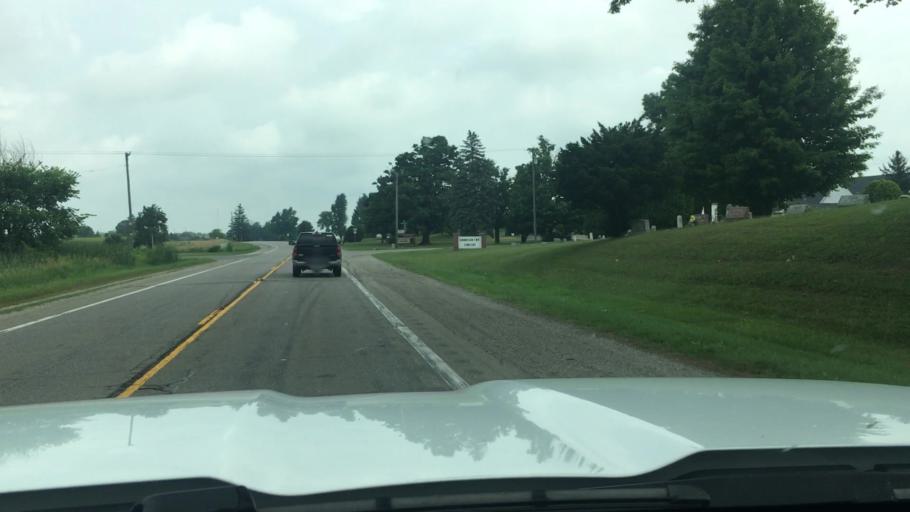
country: US
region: Michigan
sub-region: Lapeer County
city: Imlay City
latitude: 43.0938
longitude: -83.0724
